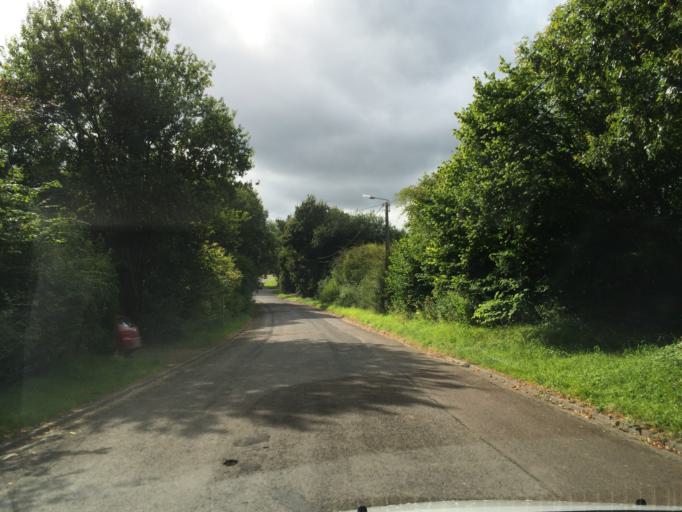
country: BE
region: Wallonia
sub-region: Province du Luxembourg
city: Chiny
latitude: 49.6946
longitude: 5.3682
